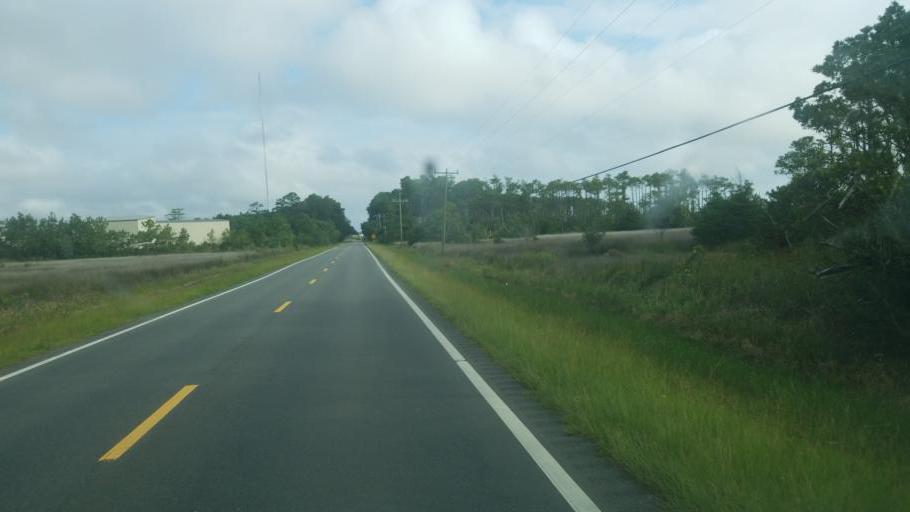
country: US
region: North Carolina
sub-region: Dare County
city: Wanchese
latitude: 35.8592
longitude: -75.6468
